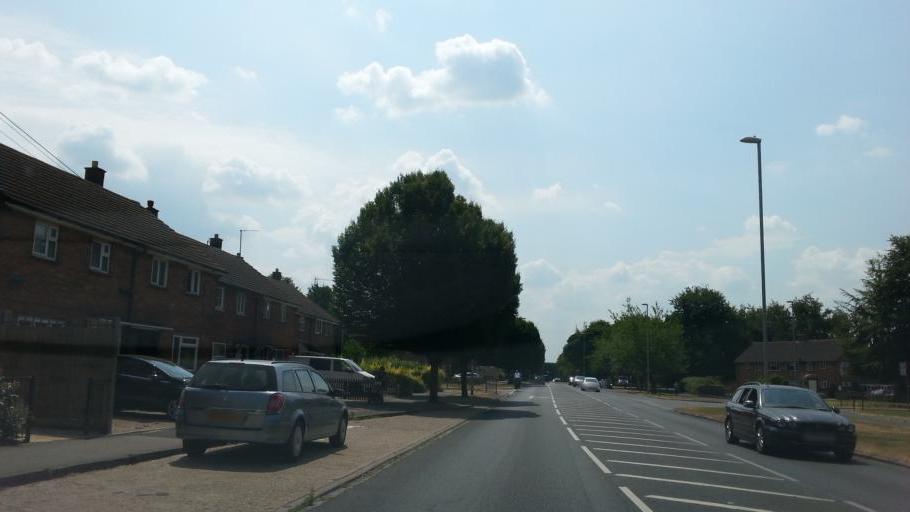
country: GB
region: England
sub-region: Cambridgeshire
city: Cambridge
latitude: 52.2106
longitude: 0.1630
